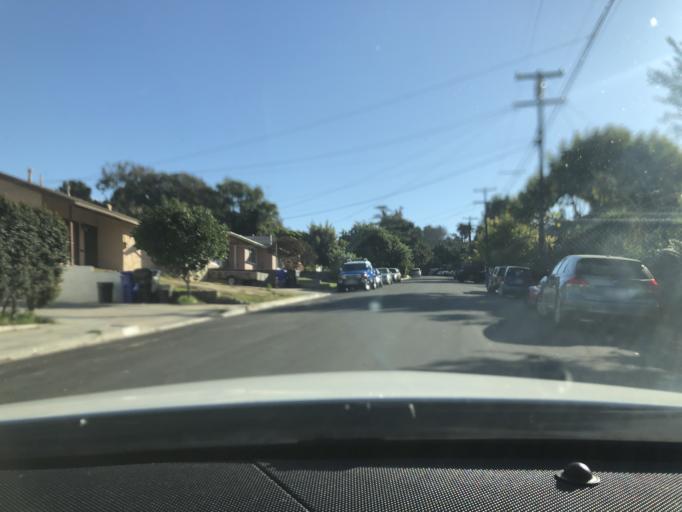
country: US
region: California
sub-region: San Diego County
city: Lemon Grove
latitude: 32.7511
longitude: -117.0662
